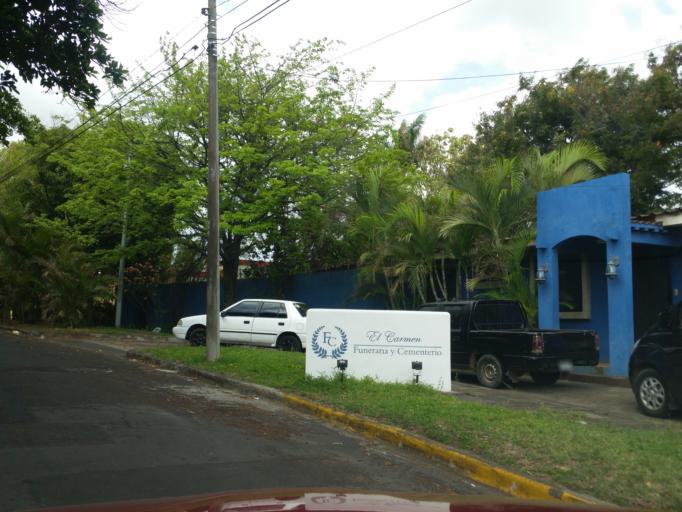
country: NI
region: Managua
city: Managua
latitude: 12.1072
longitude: -86.2645
